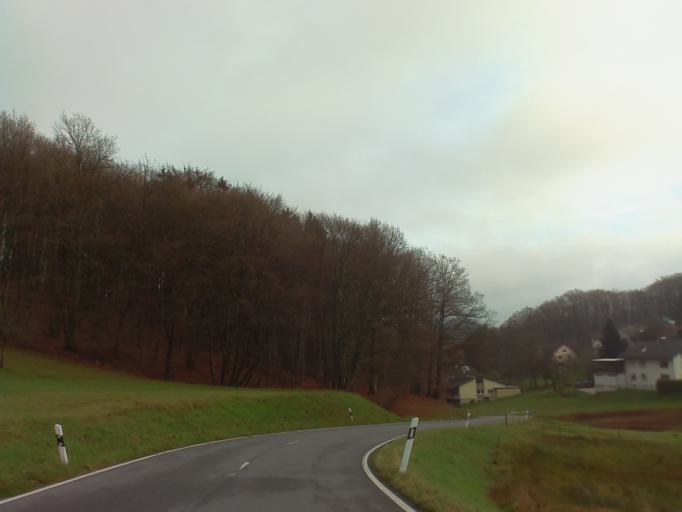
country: DE
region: Baden-Wuerttemberg
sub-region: Karlsruhe Region
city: Wilhelmsfeld
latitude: 49.4952
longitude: 8.7590
